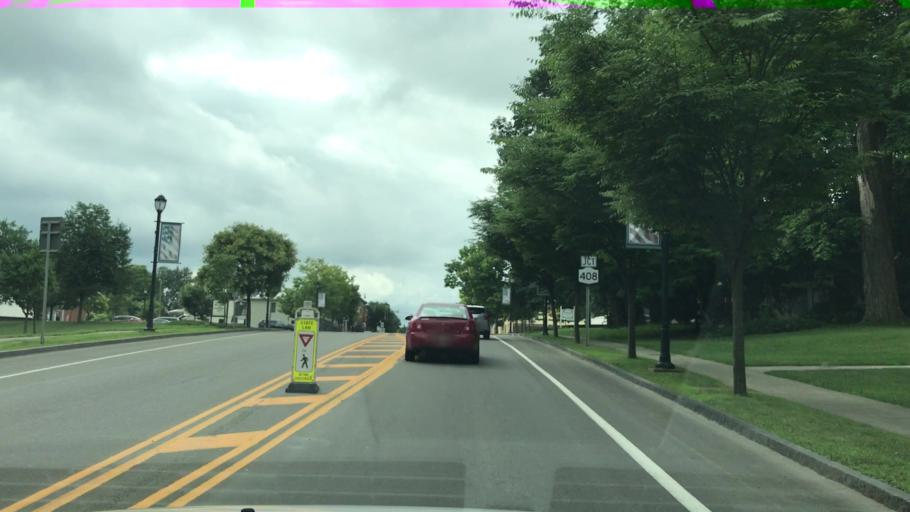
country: US
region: New York
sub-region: Livingston County
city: Mount Morris
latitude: 42.7275
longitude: -77.8752
